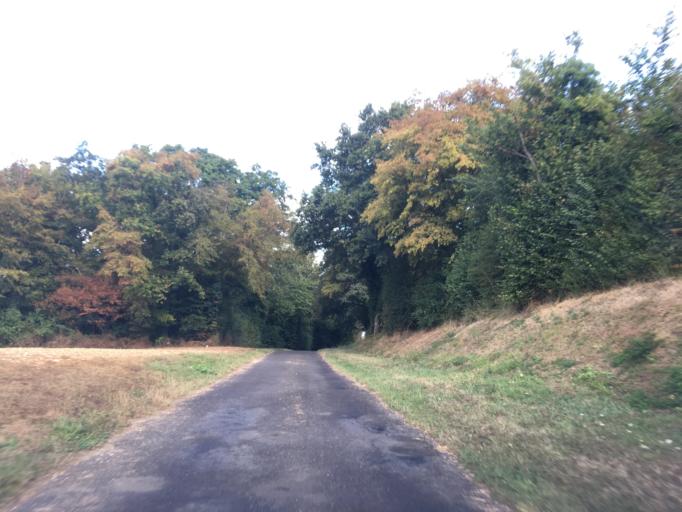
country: FR
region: Haute-Normandie
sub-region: Departement de l'Eure
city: Courcelles-sur-Seine
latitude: 49.1774
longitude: 1.3899
